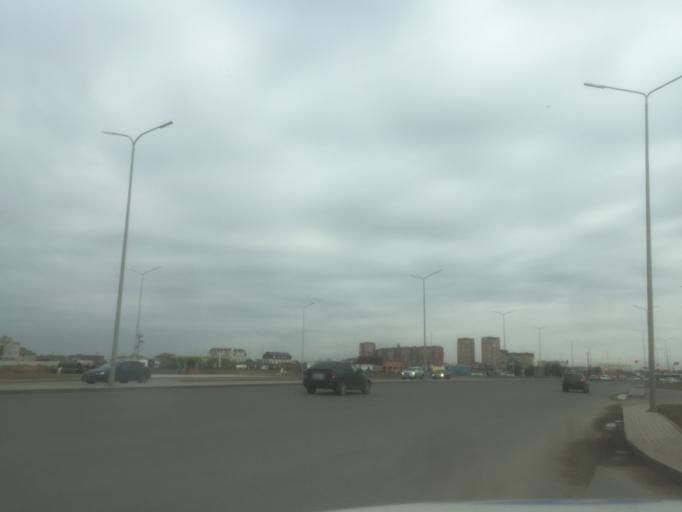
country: KZ
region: Astana Qalasy
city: Astana
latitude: 51.1699
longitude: 71.3767
